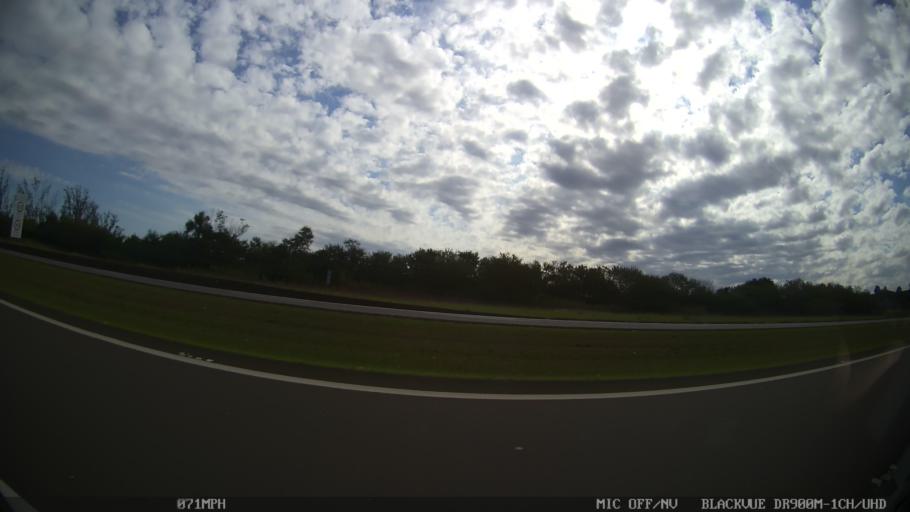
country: BR
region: Sao Paulo
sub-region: Iracemapolis
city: Iracemapolis
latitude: -22.6036
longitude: -47.4575
